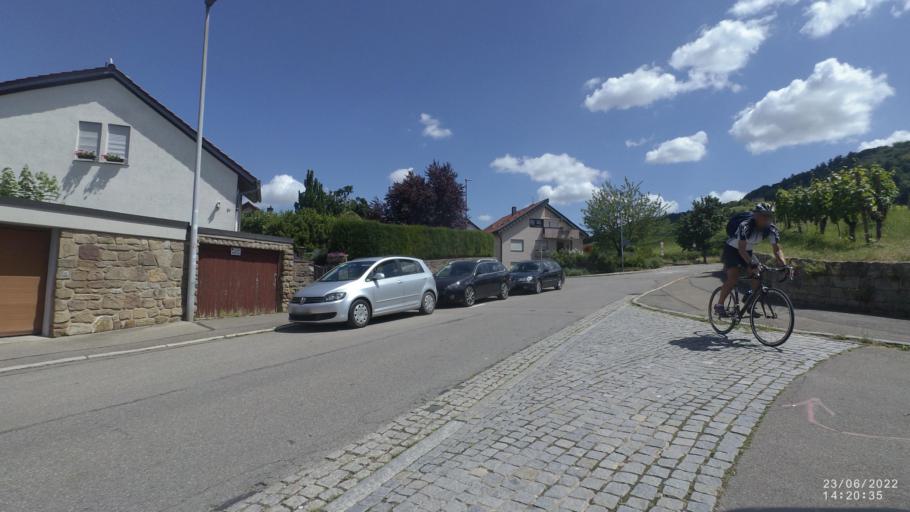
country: DE
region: Baden-Wuerttemberg
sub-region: Regierungsbezirk Stuttgart
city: Fellbach
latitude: 48.8024
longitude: 9.2811
